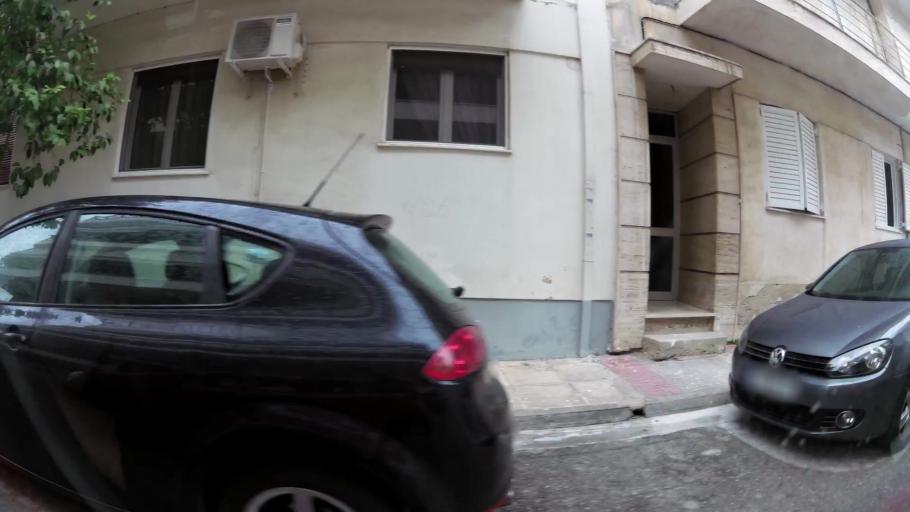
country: GR
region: Attica
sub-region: Nomarchia Athinas
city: Ilion
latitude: 38.0252
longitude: 23.7039
